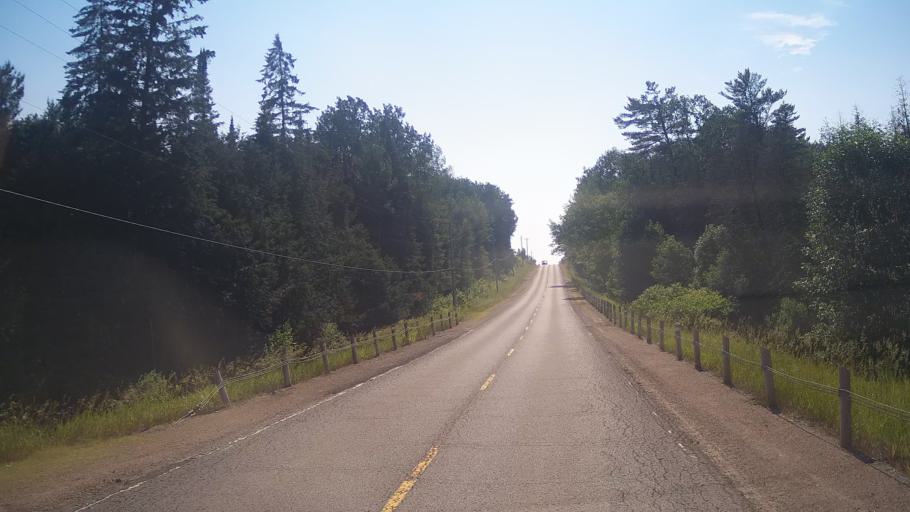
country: CA
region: Ontario
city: Pembroke
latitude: 45.6069
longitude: -77.2161
